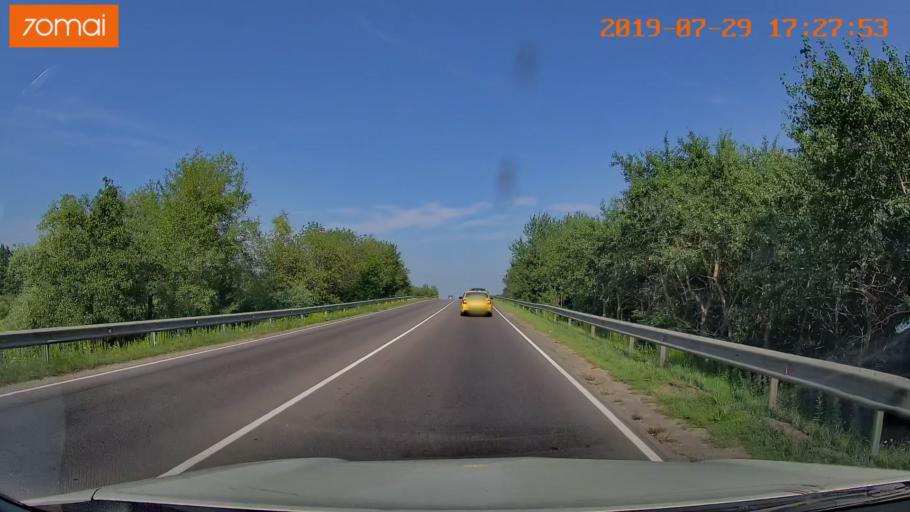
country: RU
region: Kaliningrad
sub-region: Gorod Kaliningrad
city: Kaliningrad
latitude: 54.7612
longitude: 20.4608
